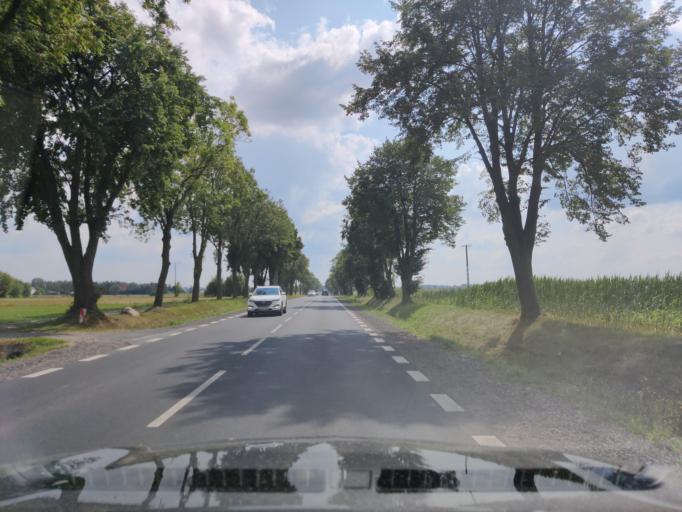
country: PL
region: Masovian Voivodeship
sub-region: Powiat pultuski
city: Zatory
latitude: 52.6143
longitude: 21.1044
